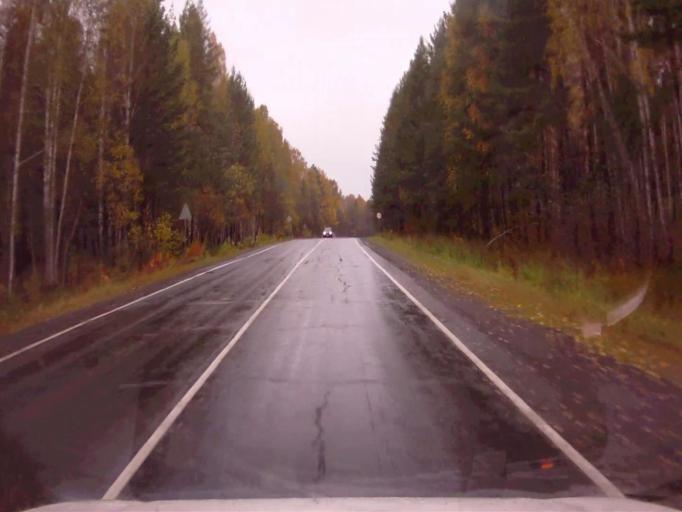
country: RU
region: Chelyabinsk
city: Verkhniy Ufaley
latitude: 55.9518
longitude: 60.3980
